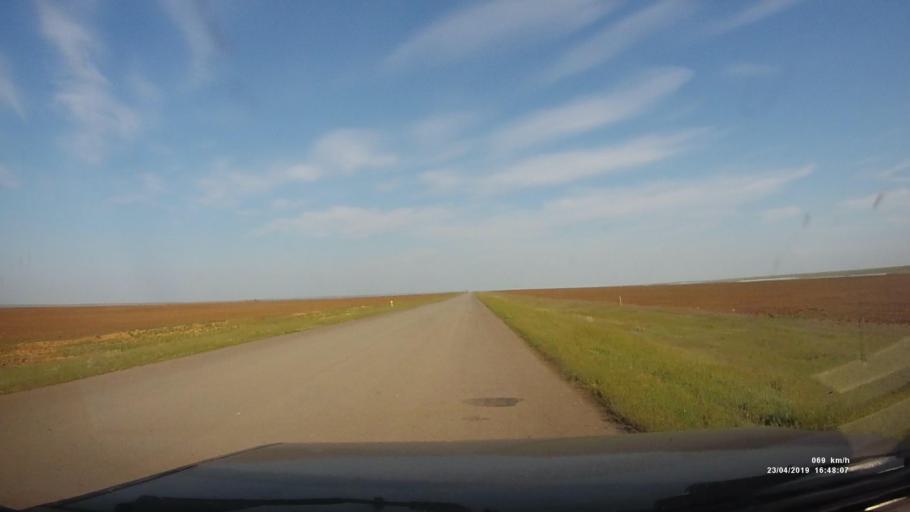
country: RU
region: Kalmykiya
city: Priyutnoye
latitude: 46.3361
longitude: 43.2574
